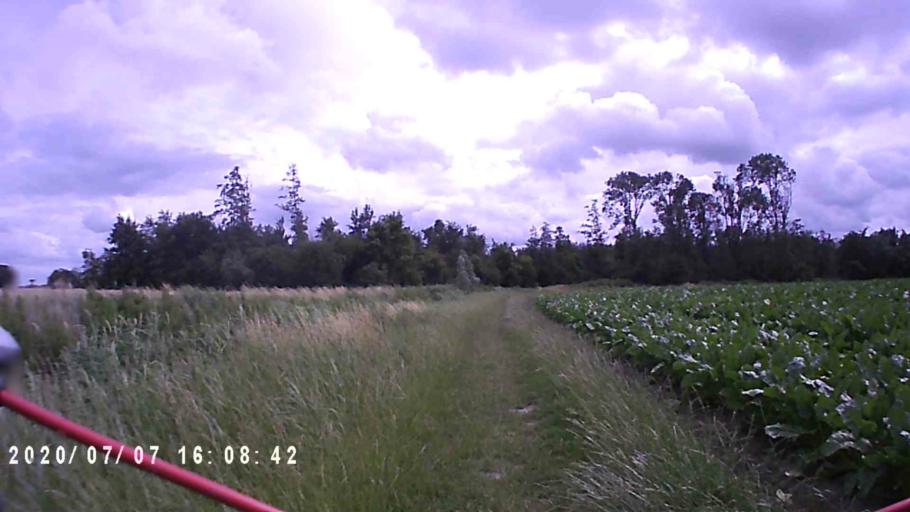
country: NL
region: Groningen
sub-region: Gemeente Winsum
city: Winsum
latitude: 53.3679
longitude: 6.5246
